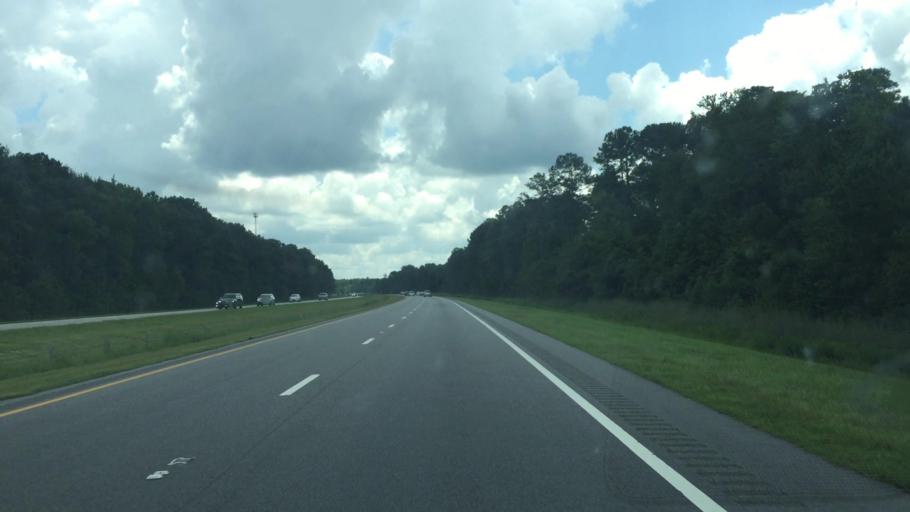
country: US
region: North Carolina
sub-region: Columbus County
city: Chadbourn
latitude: 34.4189
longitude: -78.9389
